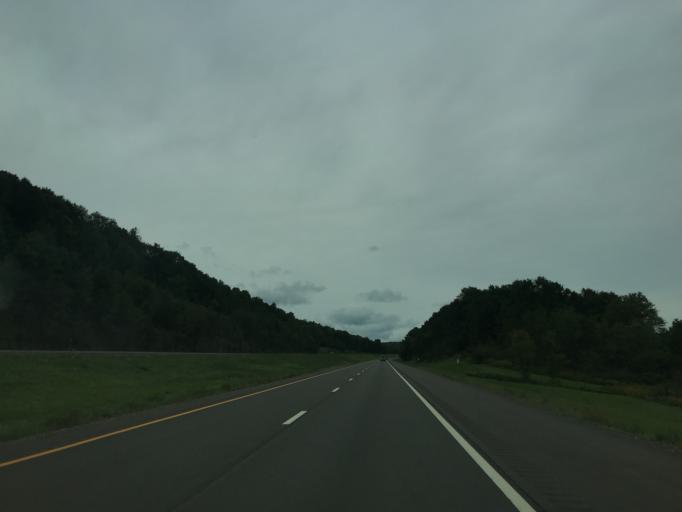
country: US
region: New York
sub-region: Broome County
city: Chenango Bridge
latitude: 42.1722
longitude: -75.7557
